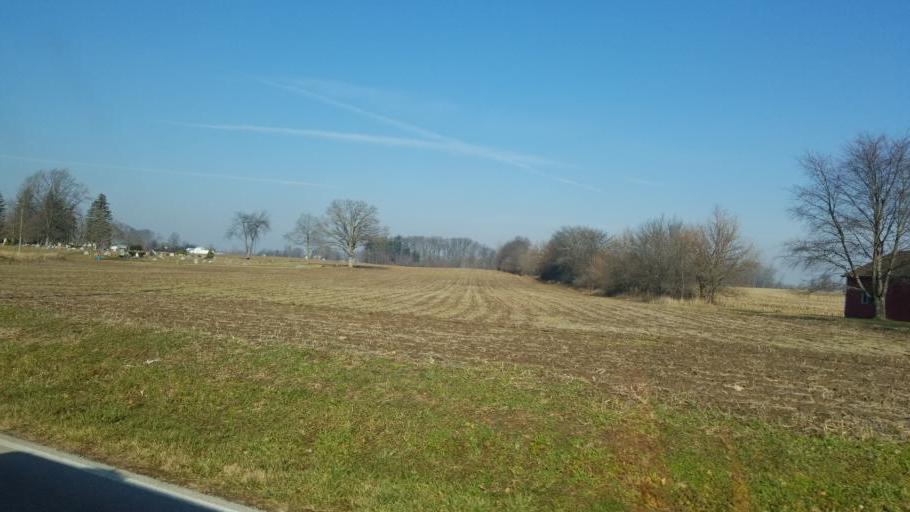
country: US
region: Ohio
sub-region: Seneca County
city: Tiffin
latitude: 41.0996
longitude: -83.1460
